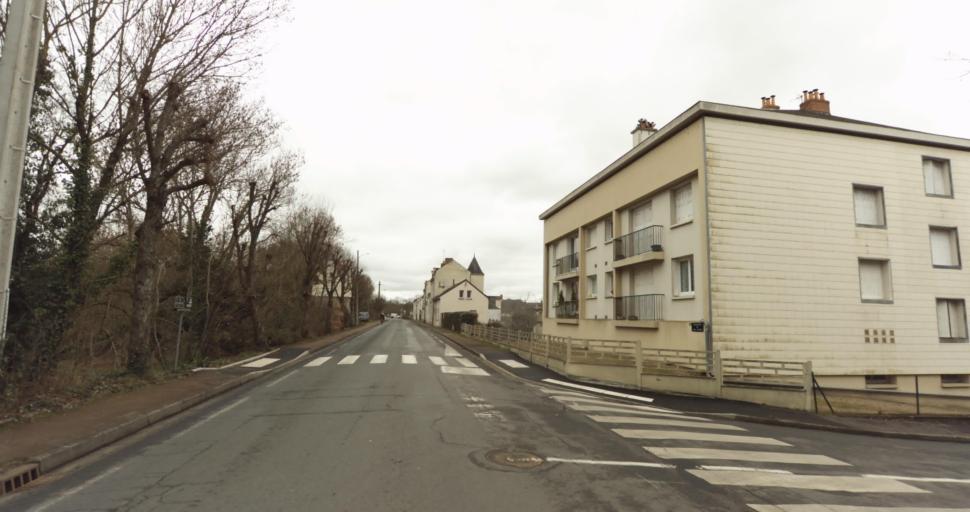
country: FR
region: Pays de la Loire
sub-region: Departement de Maine-et-Loire
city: Saumur
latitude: 47.2531
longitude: -0.0894
